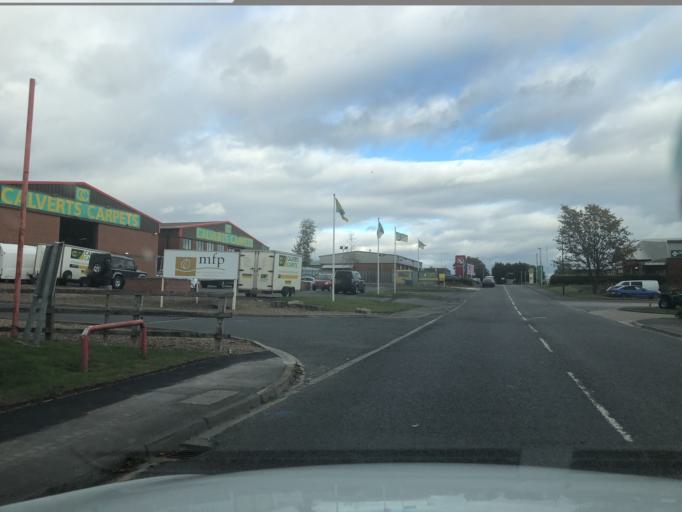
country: GB
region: England
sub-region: North Yorkshire
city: Northallerton
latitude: 54.3499
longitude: -1.4493
